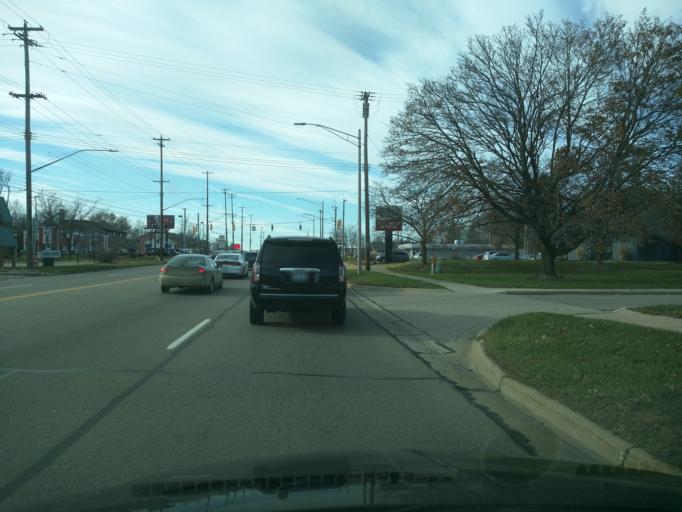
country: US
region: Michigan
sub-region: Eaton County
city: Waverly
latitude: 42.7411
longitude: -84.6121
